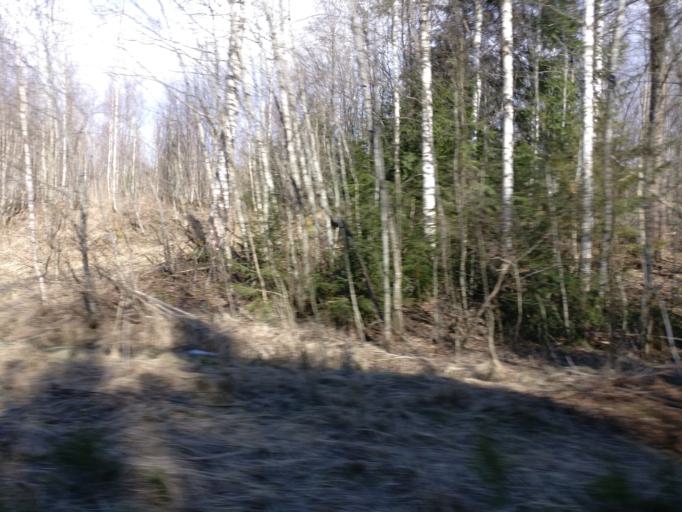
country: FI
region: Uusimaa
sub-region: Helsinki
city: Sammatti
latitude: 60.2870
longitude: 23.7670
